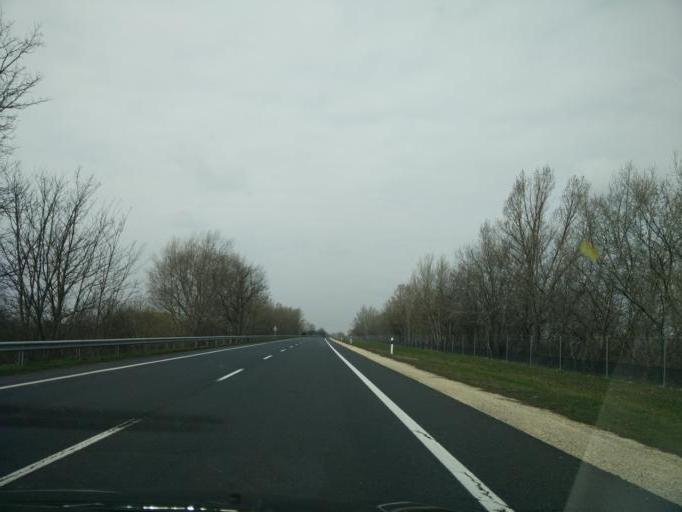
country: HU
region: Gyor-Moson-Sopron
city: Per
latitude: 47.6923
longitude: 17.7907
